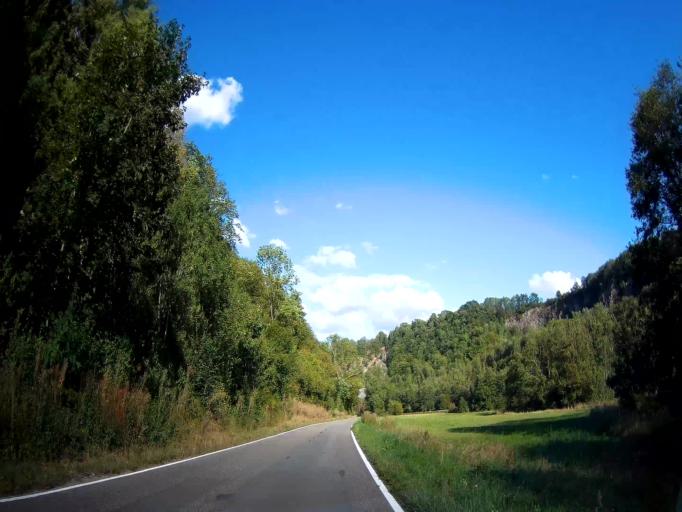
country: BE
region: Wallonia
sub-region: Province de Namur
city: Anhee
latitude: 50.3035
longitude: 4.8237
